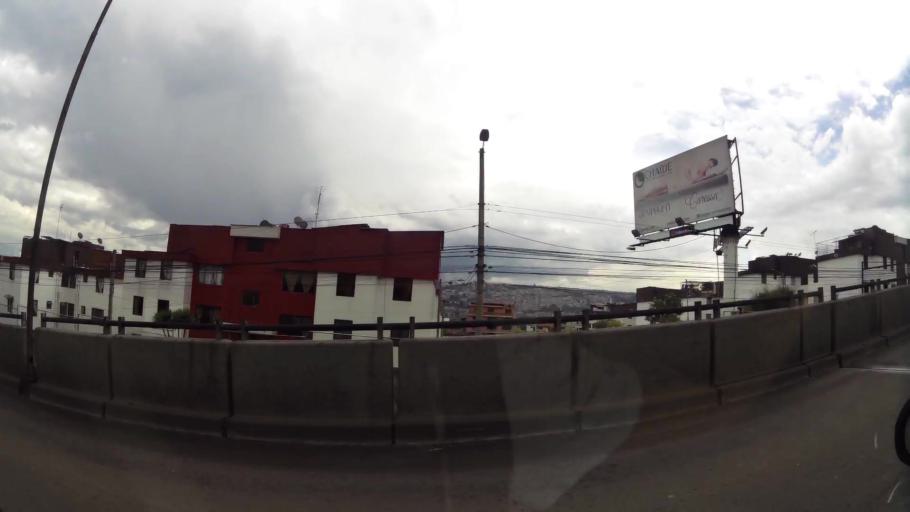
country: EC
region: Pichincha
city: Quito
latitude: -0.2776
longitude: -78.5526
